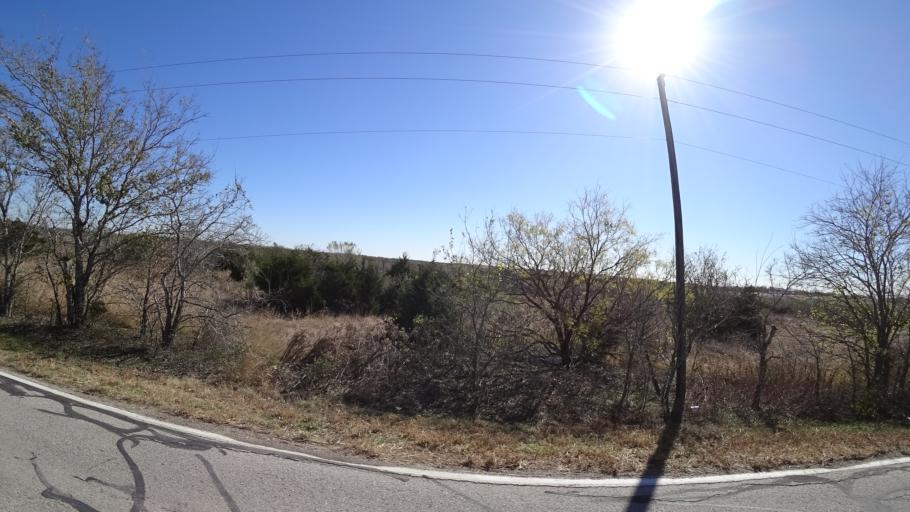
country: US
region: Texas
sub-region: Travis County
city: Garfield
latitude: 30.1011
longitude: -97.6331
